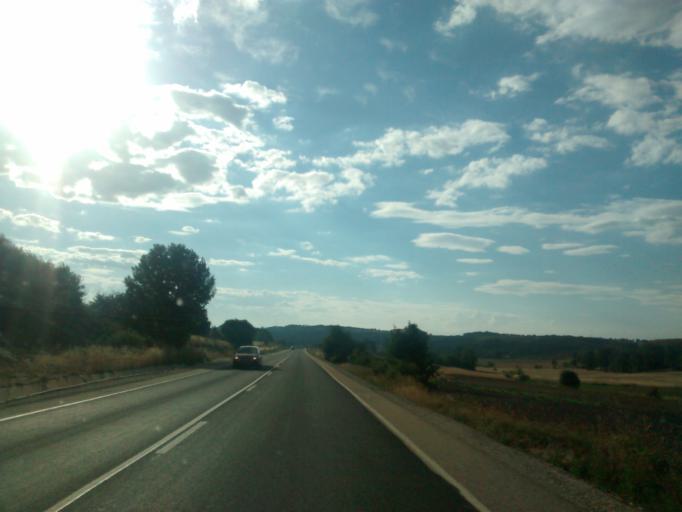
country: ES
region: Castille and Leon
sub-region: Provincia de Burgos
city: Basconcillos del Tozo
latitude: 42.6718
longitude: -3.9307
